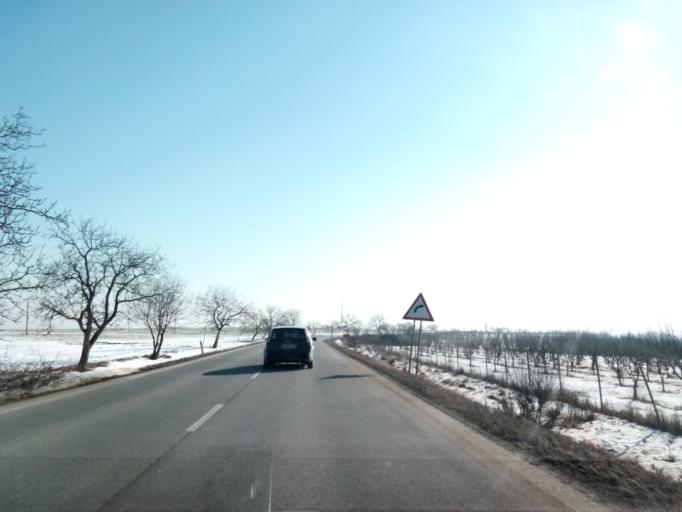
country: SK
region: Kosicky
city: Secovce
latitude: 48.7279
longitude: 21.5995
